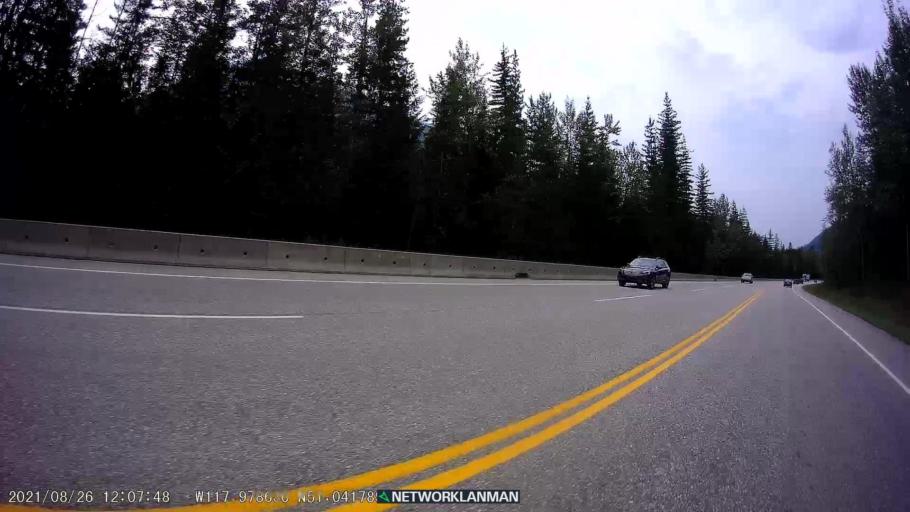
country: CA
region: British Columbia
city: Revelstoke
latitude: 51.0417
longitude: -117.9787
